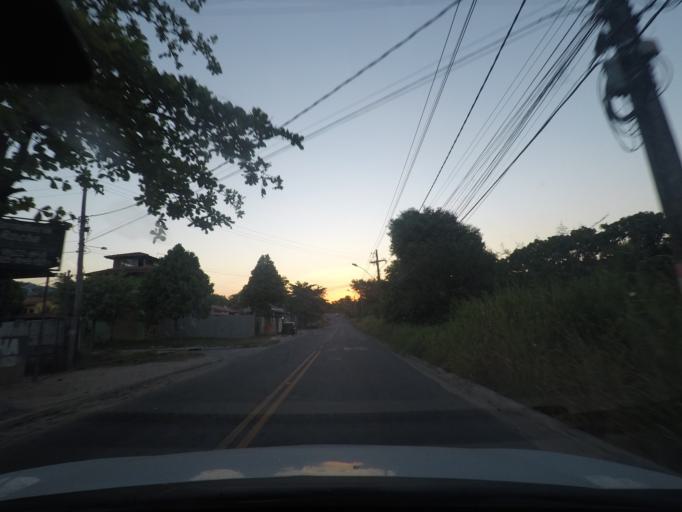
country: BR
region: Rio de Janeiro
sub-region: Sao Goncalo
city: Sao Goncalo
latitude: -22.9480
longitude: -42.9680
